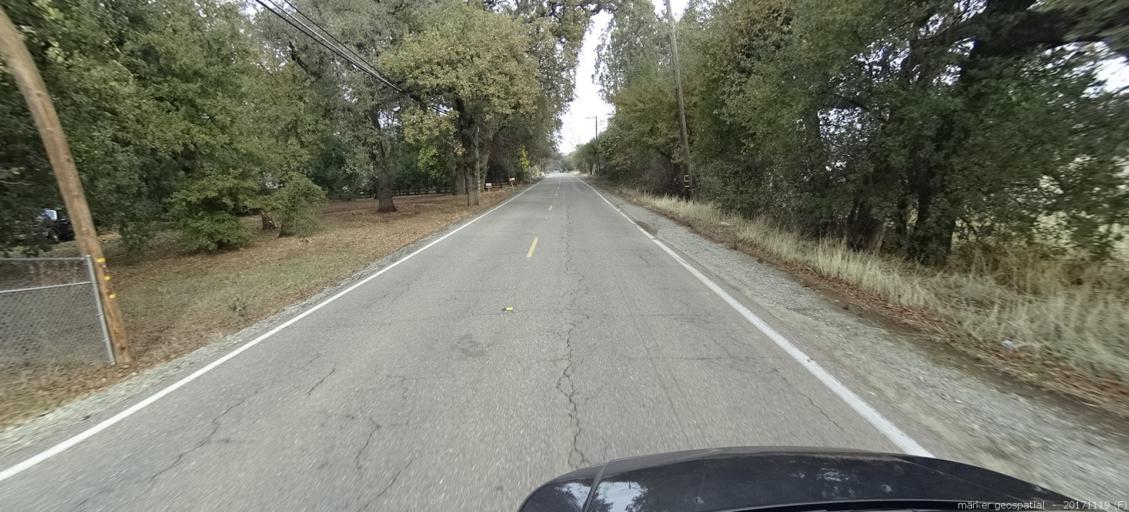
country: US
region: California
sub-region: Shasta County
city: Anderson
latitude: 40.5240
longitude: -122.3337
